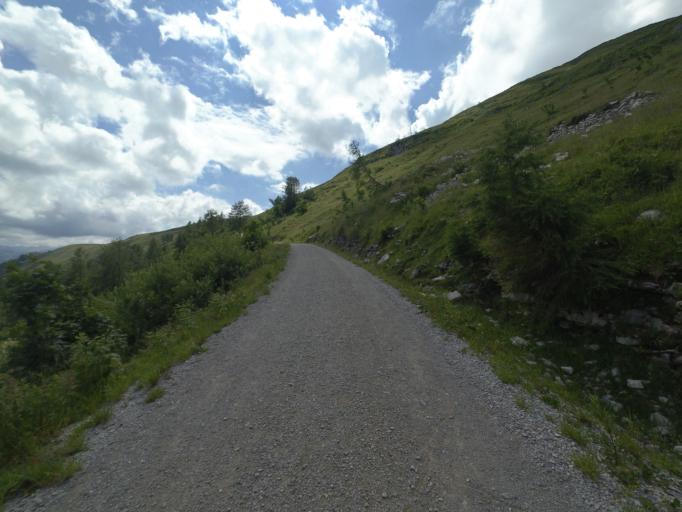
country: AT
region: Salzburg
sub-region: Politischer Bezirk Salzburg-Umgebung
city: Hintersee
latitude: 47.6583
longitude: 13.2977
